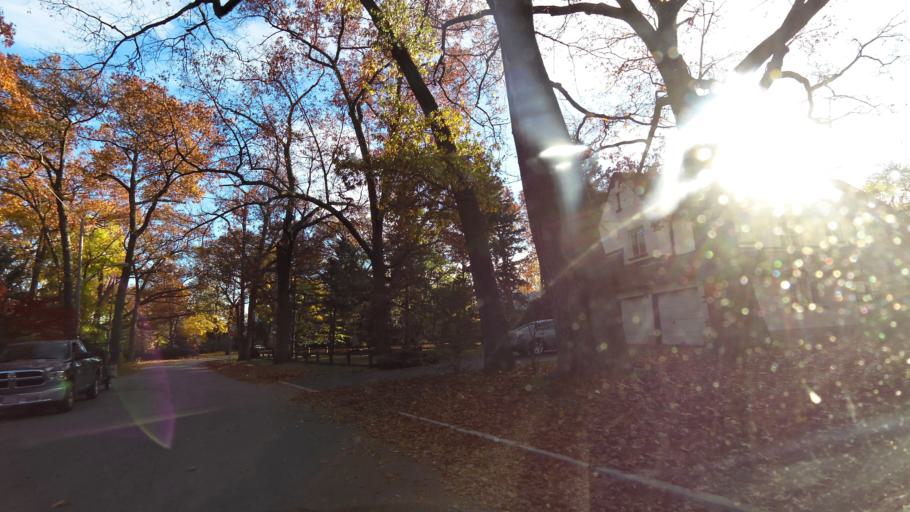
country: CA
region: Ontario
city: Etobicoke
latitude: 43.6533
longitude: -79.5048
